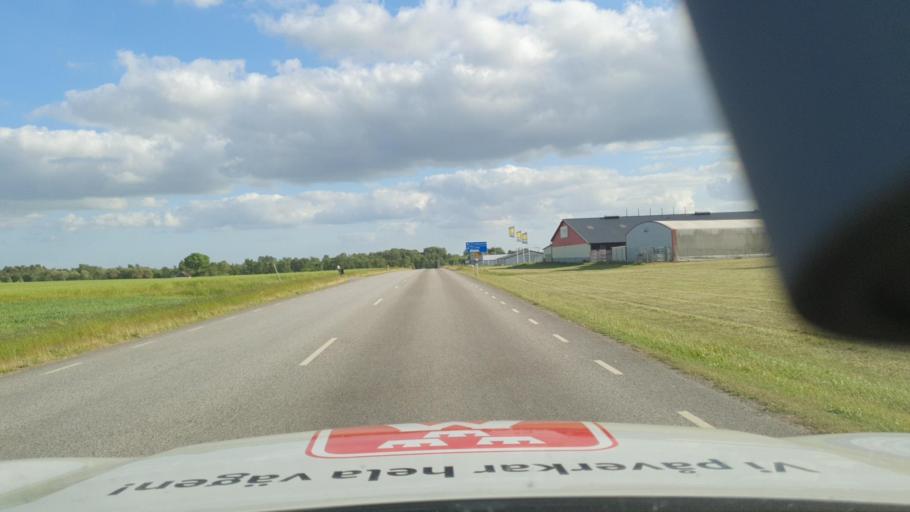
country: SE
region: Skane
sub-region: Tomelilla Kommun
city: Tomelilla
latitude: 55.5534
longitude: 13.9601
